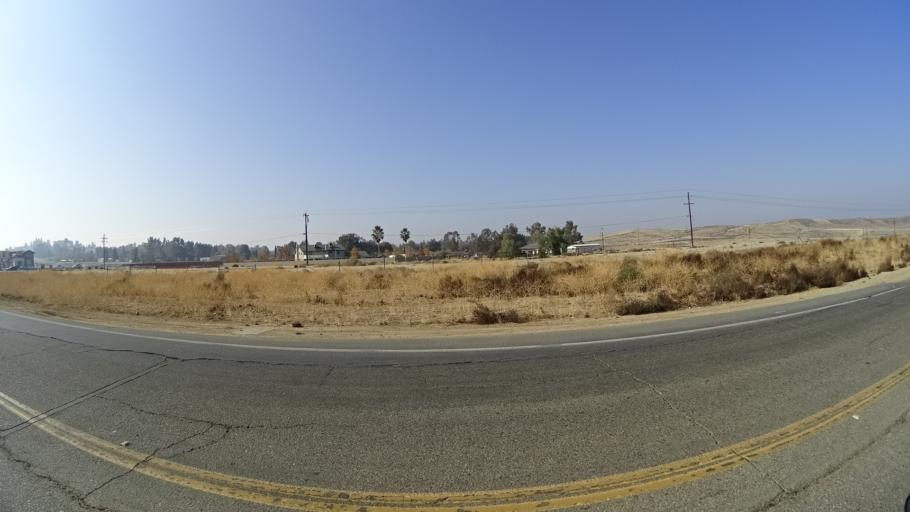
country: US
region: California
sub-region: Kern County
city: Lamont
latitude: 35.4087
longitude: -118.8597
